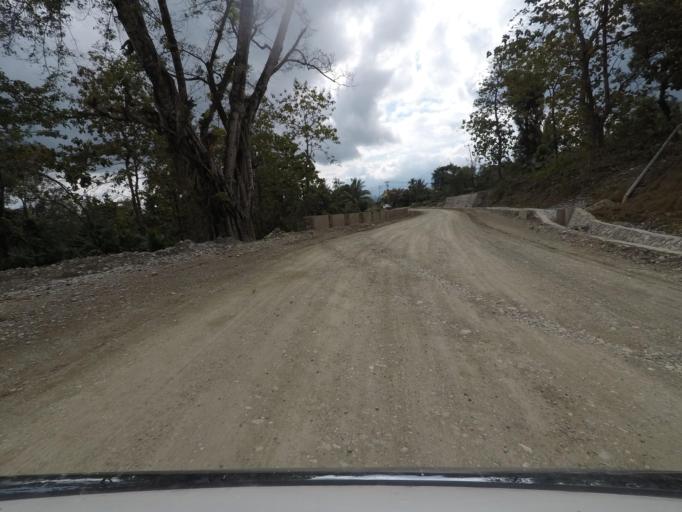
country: TL
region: Viqueque
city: Viqueque
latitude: -8.7925
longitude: 126.3769
